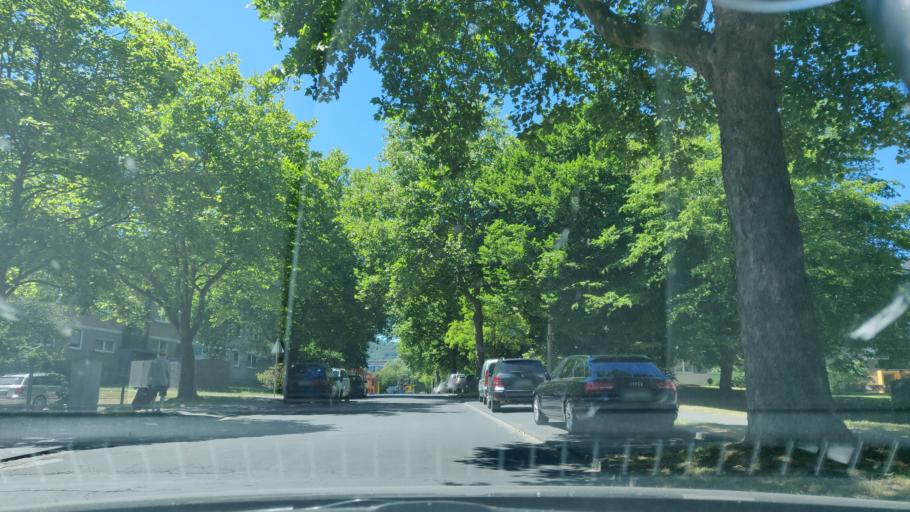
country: DE
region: Hesse
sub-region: Regierungsbezirk Kassel
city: Fuldabruck
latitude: 51.2802
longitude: 9.4456
